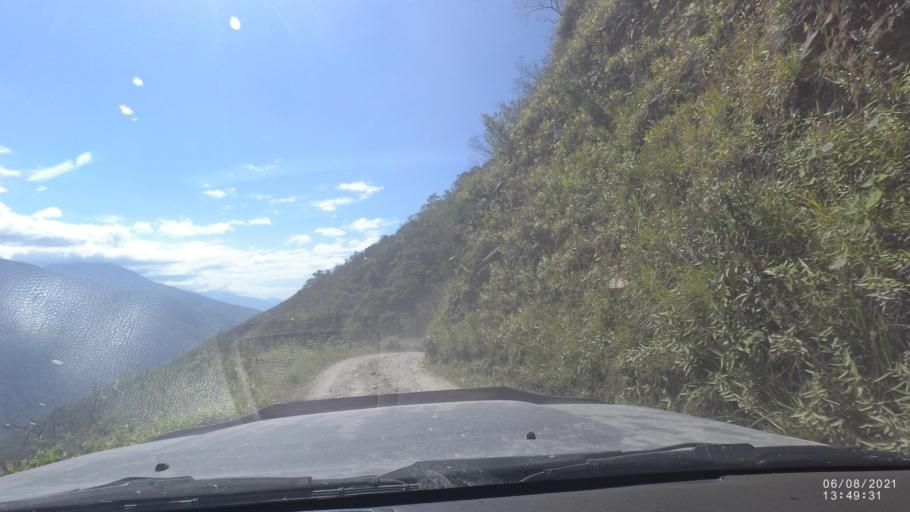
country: BO
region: La Paz
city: Quime
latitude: -16.6606
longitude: -66.7218
